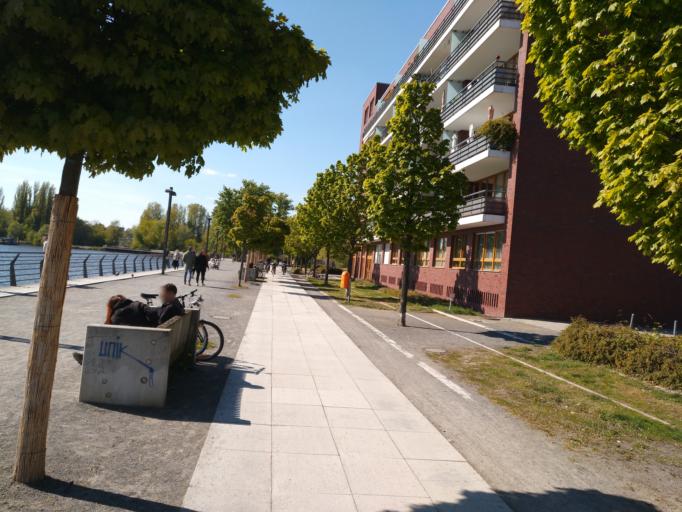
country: DE
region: Berlin
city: Rummelsburg
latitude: 52.4995
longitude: 13.4761
